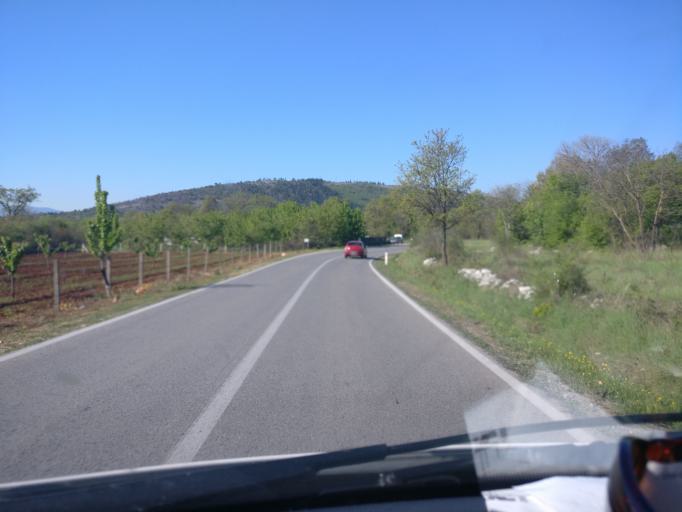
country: BA
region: Federation of Bosnia and Herzegovina
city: Tasovcici
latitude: 43.1240
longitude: 17.7522
